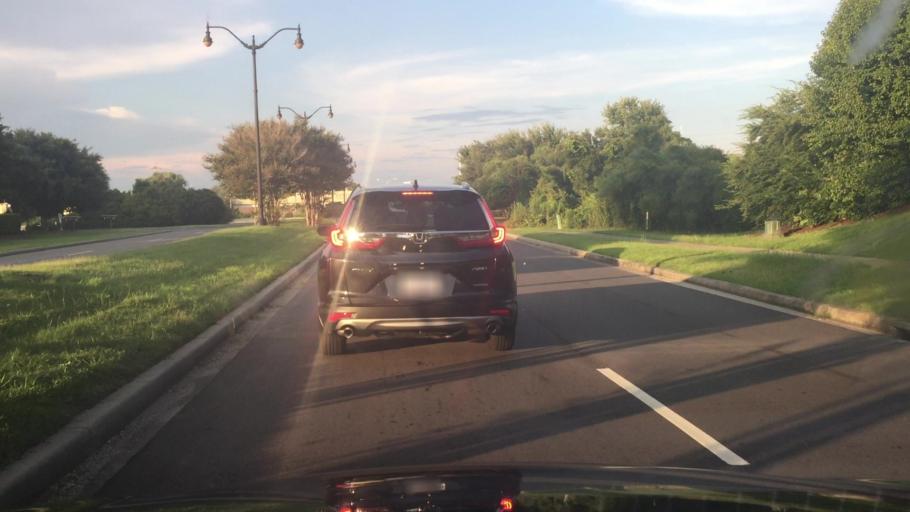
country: US
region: South Carolina
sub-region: Horry County
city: Forestbrook
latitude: 33.7127
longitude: -78.9293
